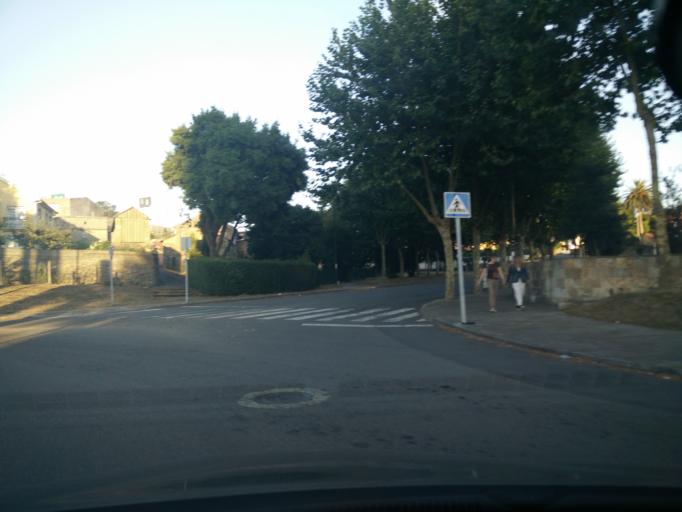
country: ES
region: Galicia
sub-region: Provincia da Coruna
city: A Coruna
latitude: 43.3349
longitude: -8.4063
